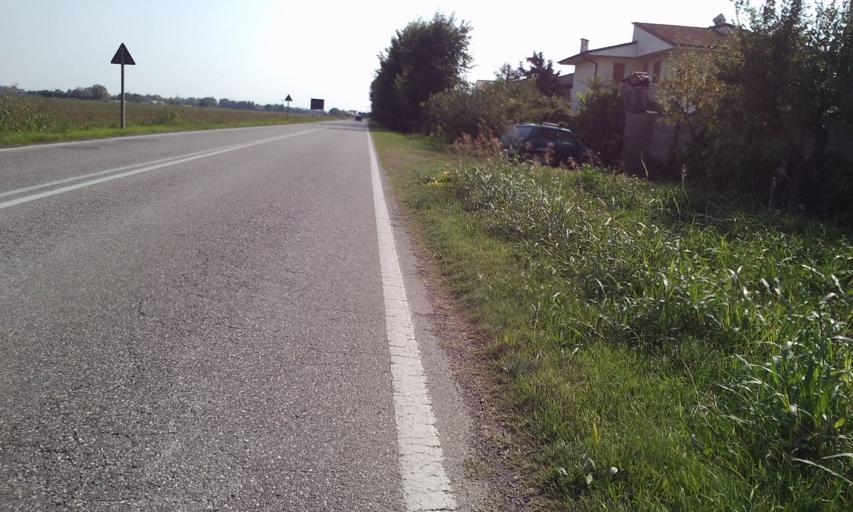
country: IT
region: Veneto
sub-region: Provincia di Verona
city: Povegliano Veronese
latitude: 45.3490
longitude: 10.8885
